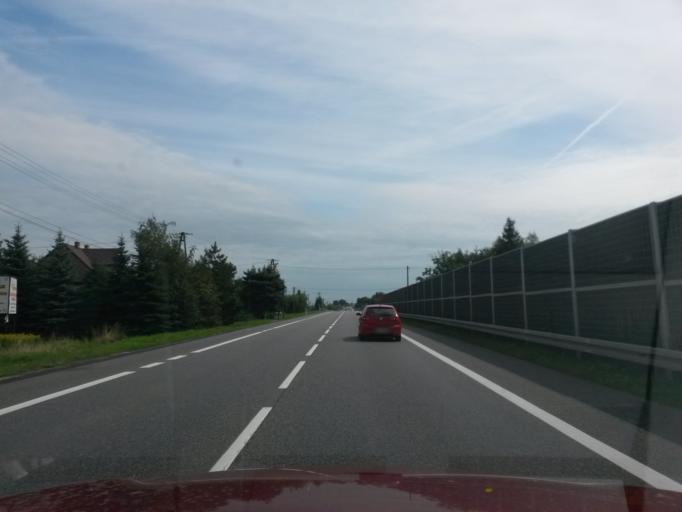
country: PL
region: Lesser Poland Voivodeship
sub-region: Powiat brzeski
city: Jasien
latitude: 49.9735
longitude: 20.5681
